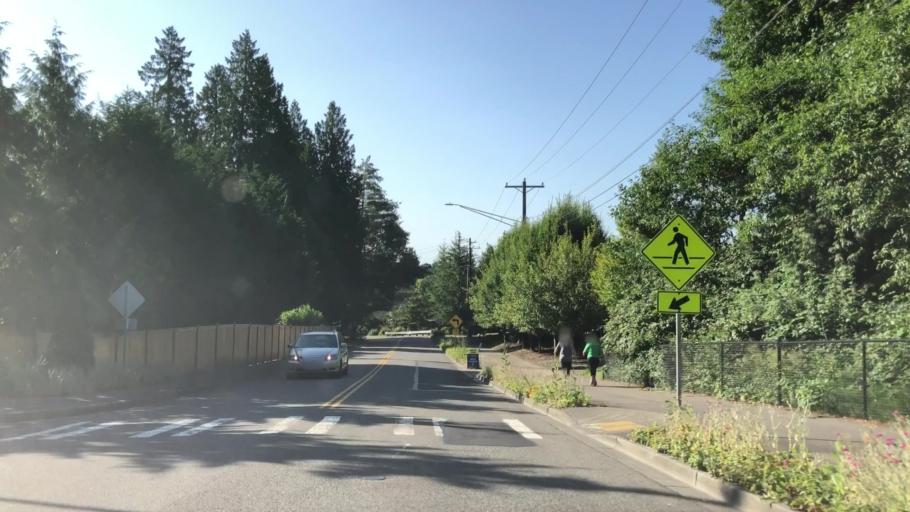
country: US
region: Washington
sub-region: King County
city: Bothell
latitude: 47.7810
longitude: -122.1921
